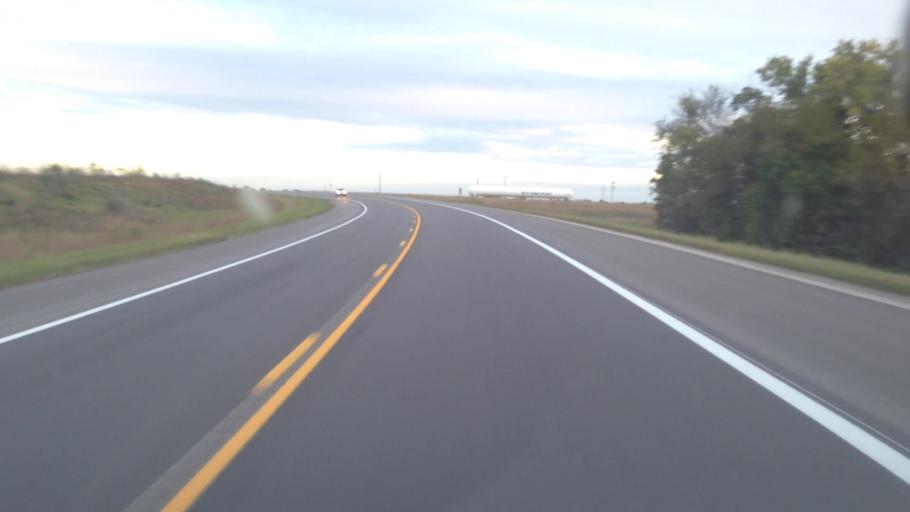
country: US
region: Kansas
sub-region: Franklin County
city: Ottawa
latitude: 38.4734
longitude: -95.2667
